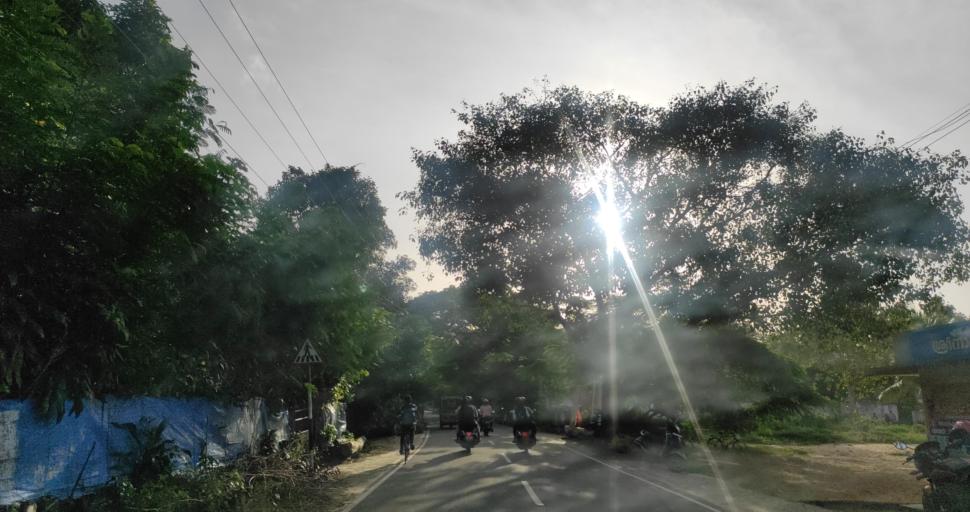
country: IN
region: Kerala
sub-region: Alappuzha
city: Shertallai
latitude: 9.6018
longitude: 76.3092
